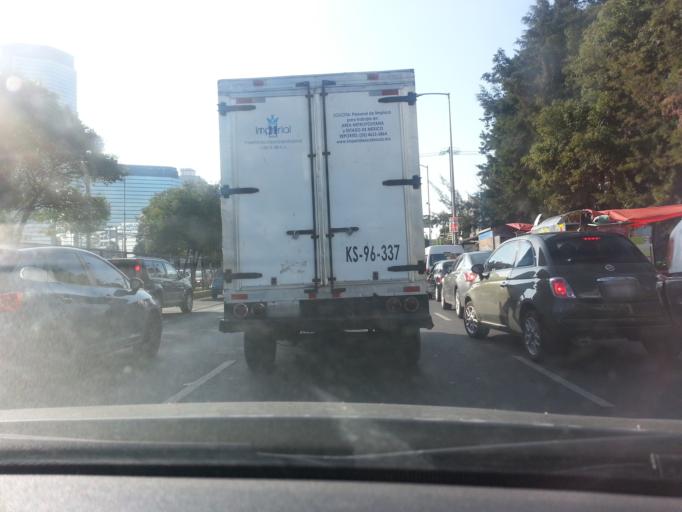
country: MX
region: Mexico City
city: Alvaro Obregon
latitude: 19.3683
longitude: -99.1817
